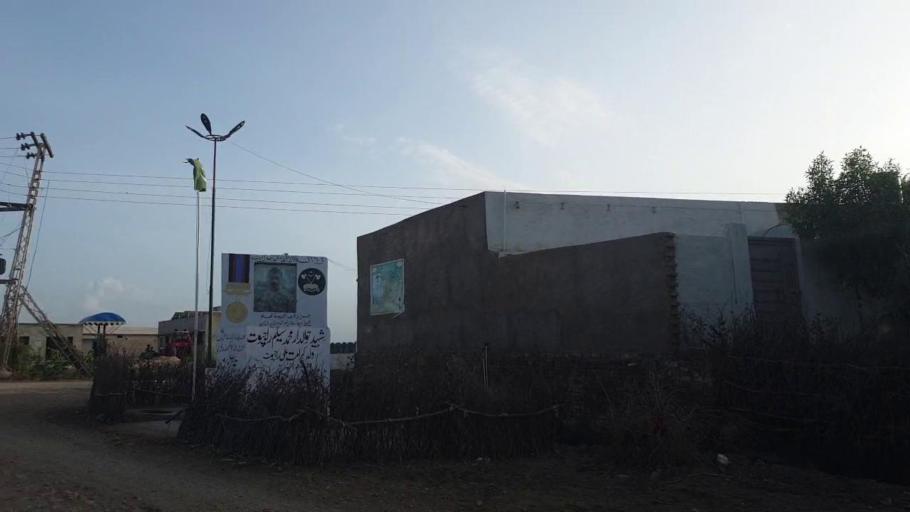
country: PK
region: Sindh
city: Kadhan
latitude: 24.6327
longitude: 69.1160
